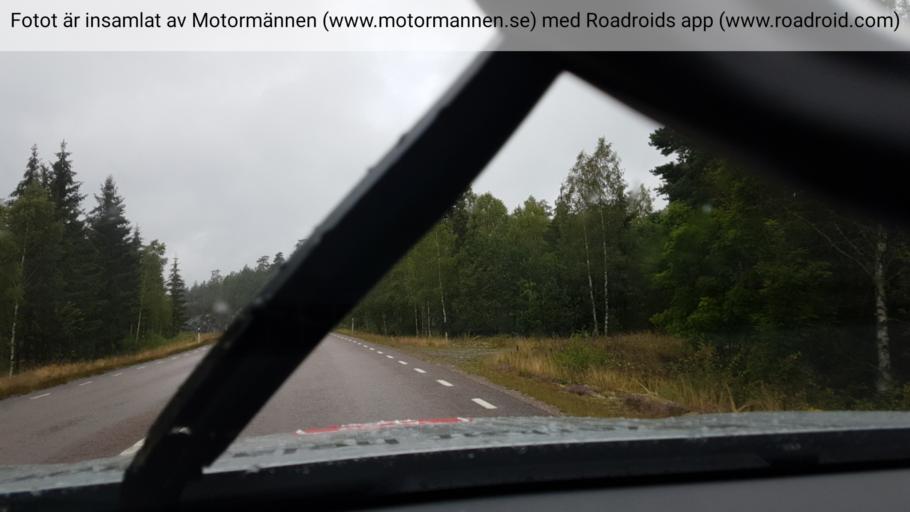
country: SE
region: Vaestra Goetaland
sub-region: Amals Kommun
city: Amal
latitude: 59.0793
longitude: 12.6246
